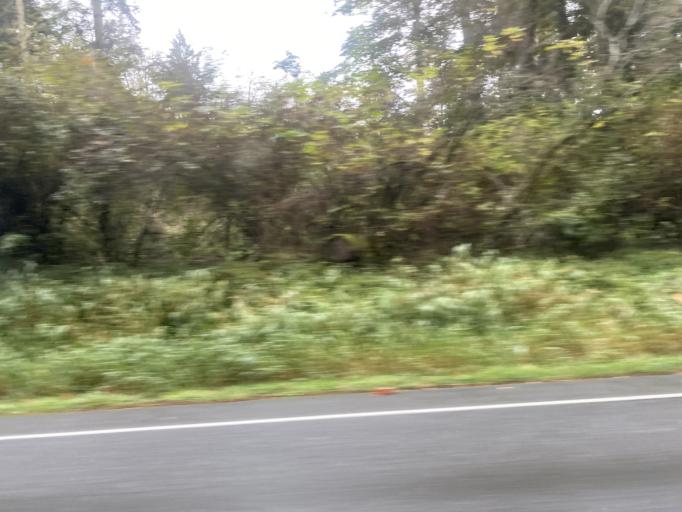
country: US
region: Washington
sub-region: Island County
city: Freeland
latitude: 48.0457
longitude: -122.5068
